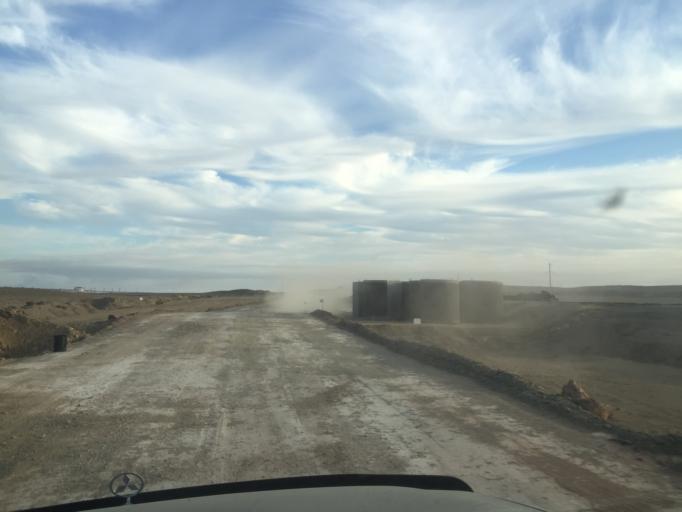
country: KZ
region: Almaty Oblysy
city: Ulken
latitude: 45.1829
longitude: 73.9228
